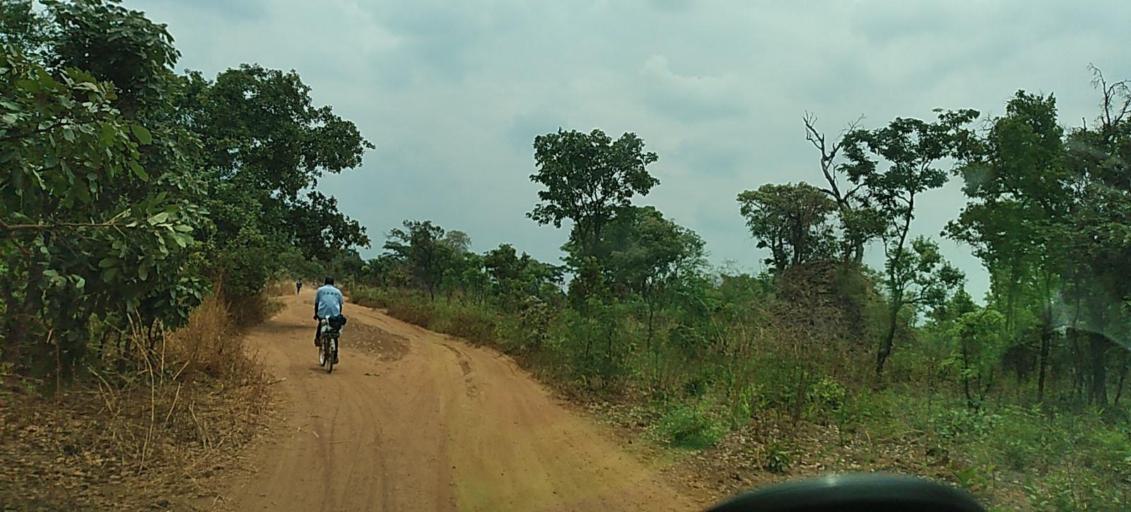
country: ZM
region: North-Western
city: Kansanshi
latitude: -12.0658
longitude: 26.3525
